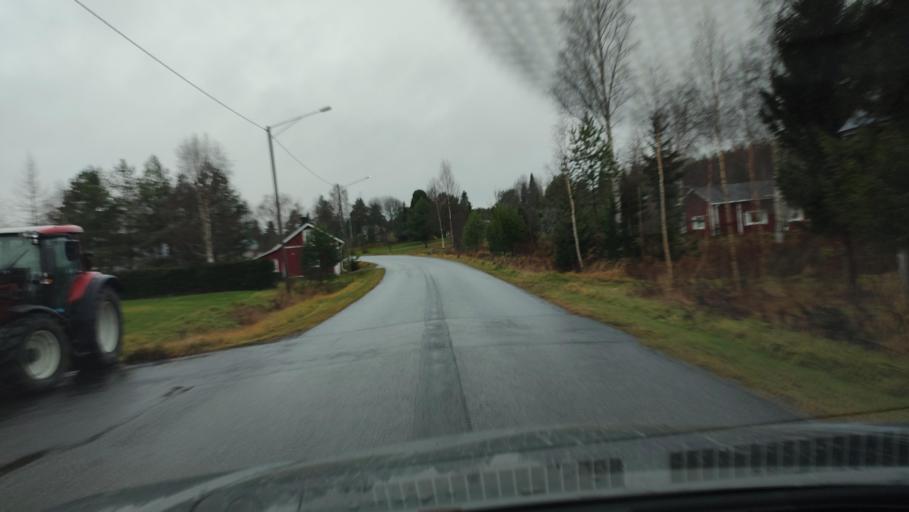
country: FI
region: Ostrobothnia
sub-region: Sydosterbotten
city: Kristinestad
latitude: 62.2644
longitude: 21.4755
